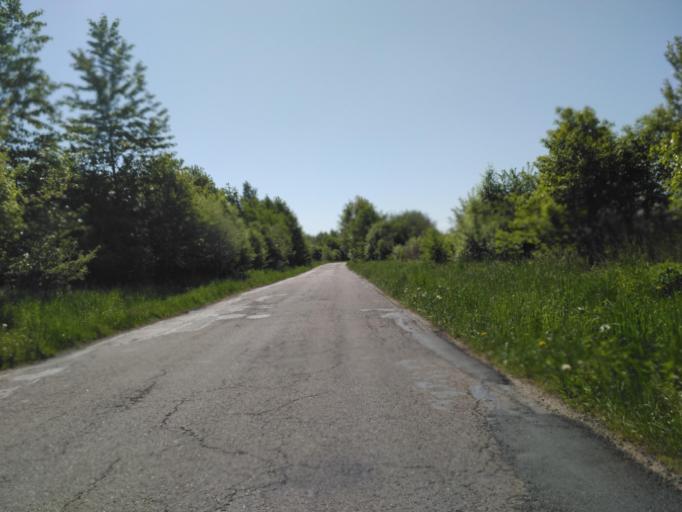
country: PL
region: Subcarpathian Voivodeship
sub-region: Powiat krosnienski
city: Miejsce Piastowe
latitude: 49.6659
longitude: 21.7969
